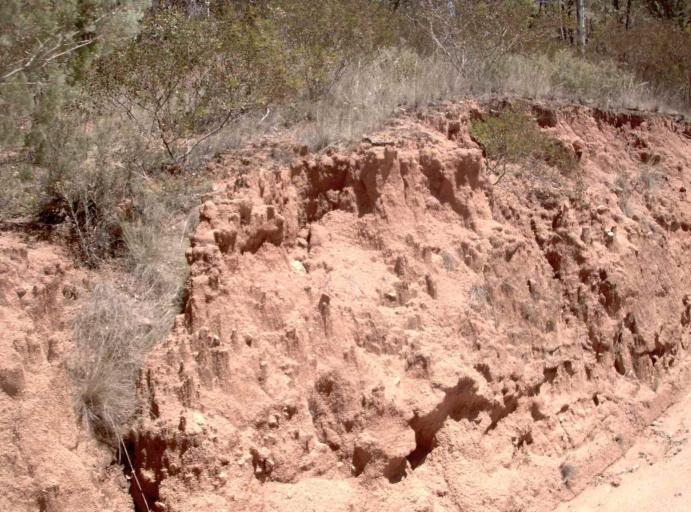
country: AU
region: New South Wales
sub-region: Snowy River
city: Jindabyne
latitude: -36.9109
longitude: 148.4177
